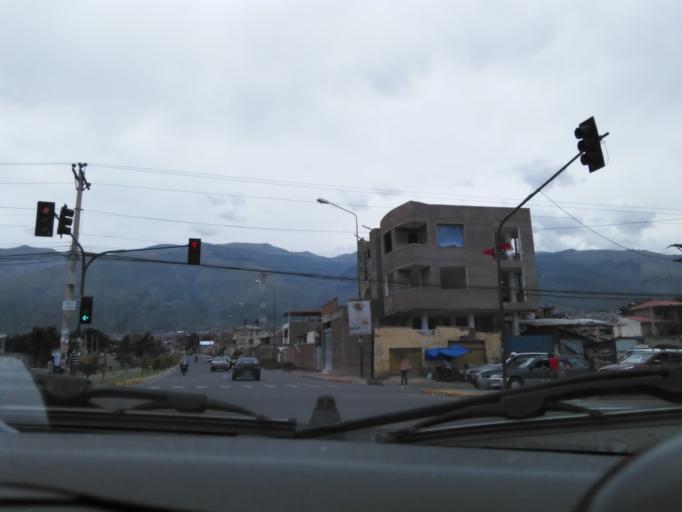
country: BO
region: Cochabamba
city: Cochabamba
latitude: -17.3646
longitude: -66.1784
